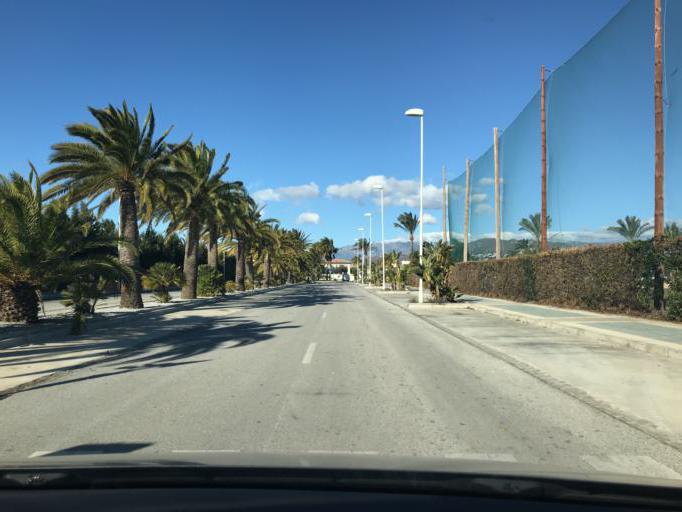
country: ES
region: Andalusia
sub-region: Provincia de Granada
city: Salobrena
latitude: 36.7203
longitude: -3.5614
